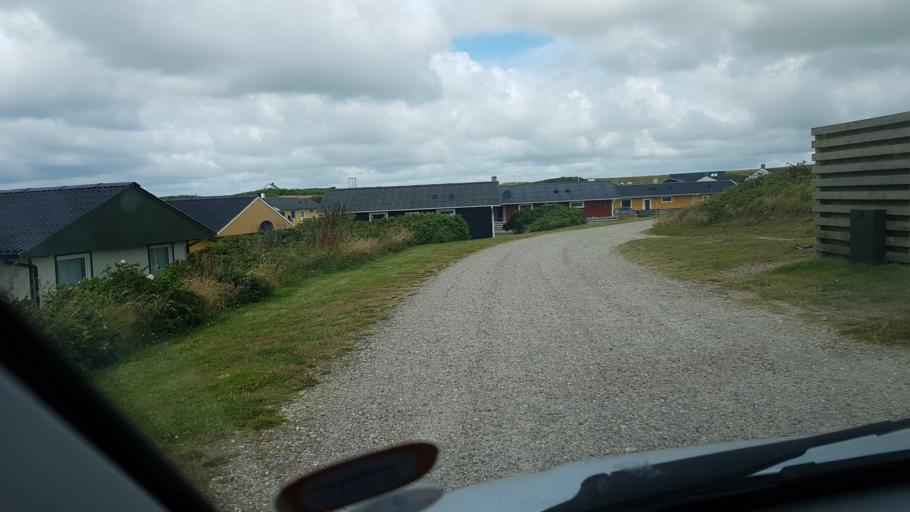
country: DK
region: Central Jutland
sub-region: Lemvig Kommune
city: Harboore
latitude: 56.4933
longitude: 8.1251
